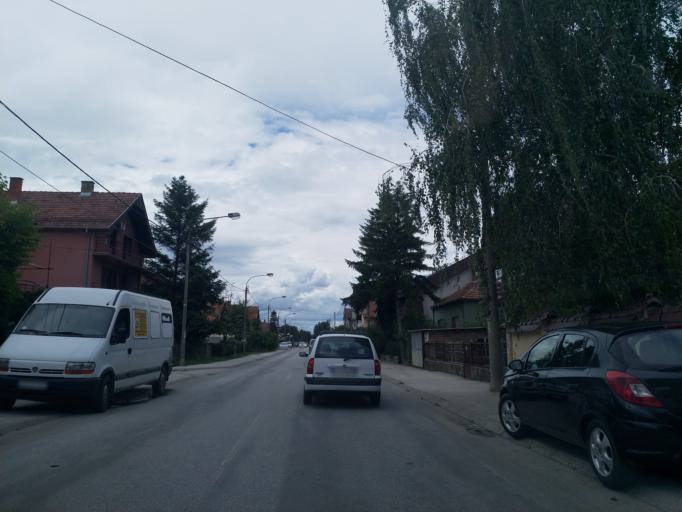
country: RS
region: Central Serbia
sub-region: Pomoravski Okrug
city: Jagodina
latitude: 43.9707
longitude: 21.2747
